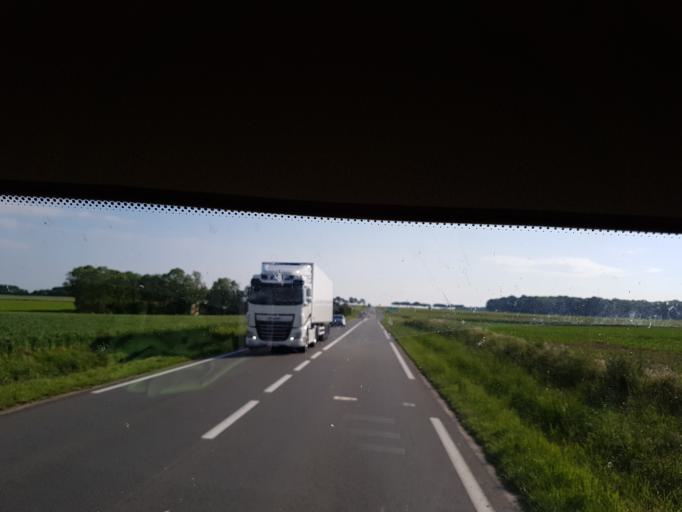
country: FR
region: Picardie
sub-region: Departement de la Somme
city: Crecy-en-Ponthieu
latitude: 50.2156
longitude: 1.9143
